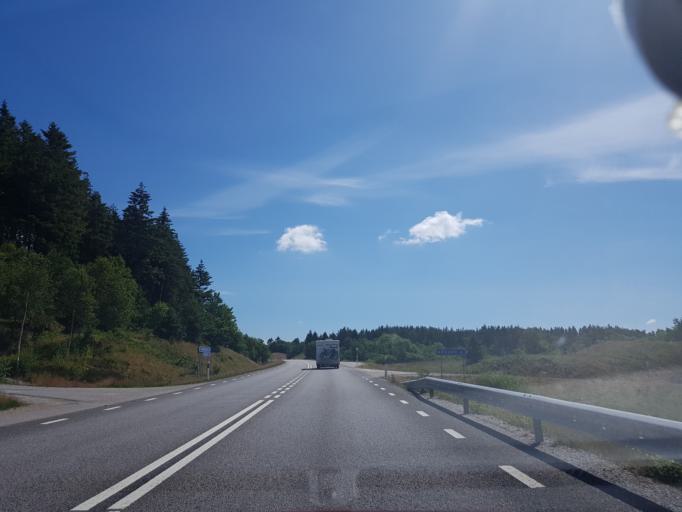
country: SE
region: Vaestra Goetaland
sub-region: Lysekils Kommun
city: Lysekil
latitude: 58.1543
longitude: 11.5290
